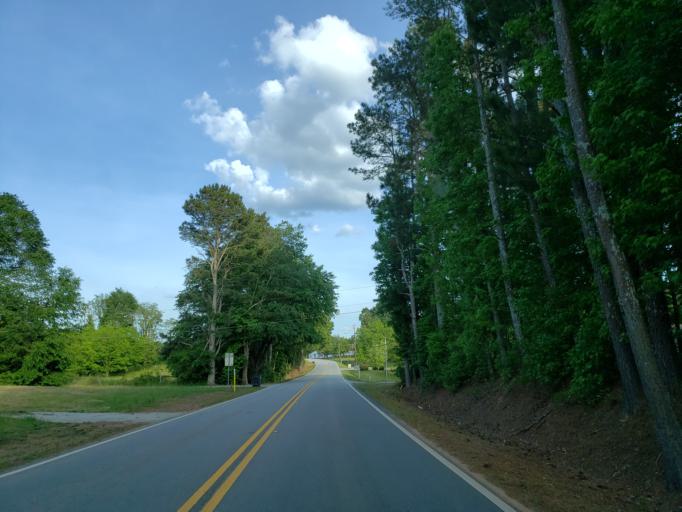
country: US
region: Georgia
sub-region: Carroll County
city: Mount Zion
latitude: 33.6359
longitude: -85.1901
